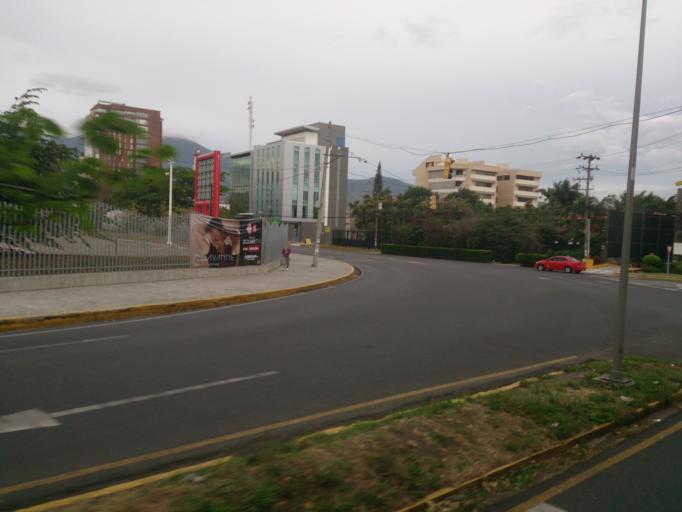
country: CR
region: San Jose
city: San Jose
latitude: 9.9385
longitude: -84.1086
